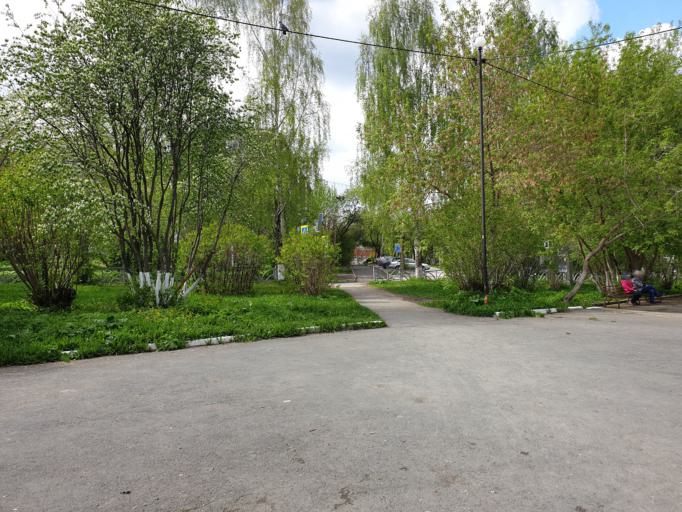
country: RU
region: Sverdlovsk
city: Pervoural'sk
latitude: 56.9119
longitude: 59.9440
